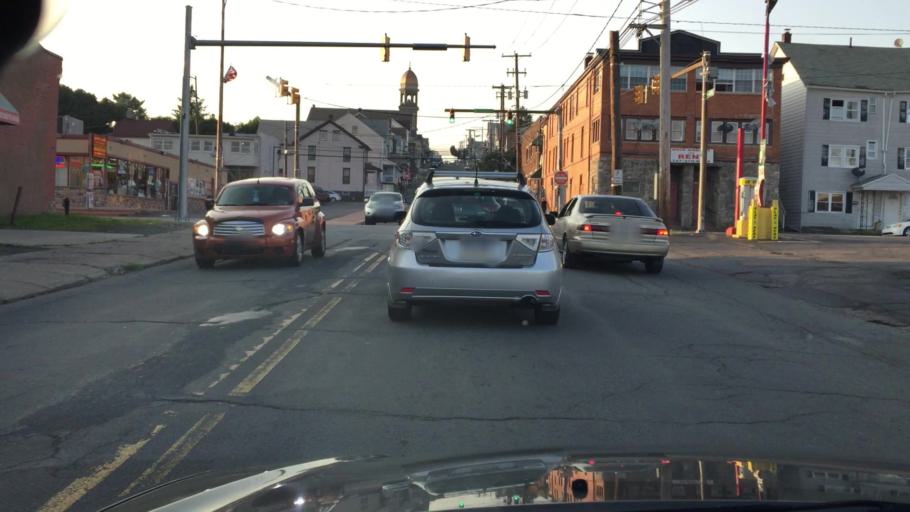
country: US
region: Pennsylvania
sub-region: Luzerne County
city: Hazleton
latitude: 40.9607
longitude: -75.9676
